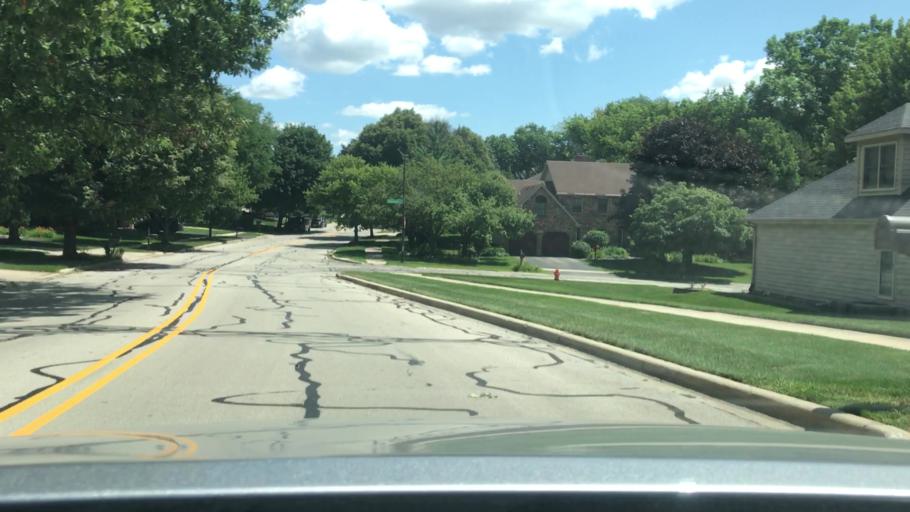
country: US
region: Illinois
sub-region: DuPage County
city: Naperville
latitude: 41.7625
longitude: -88.1185
